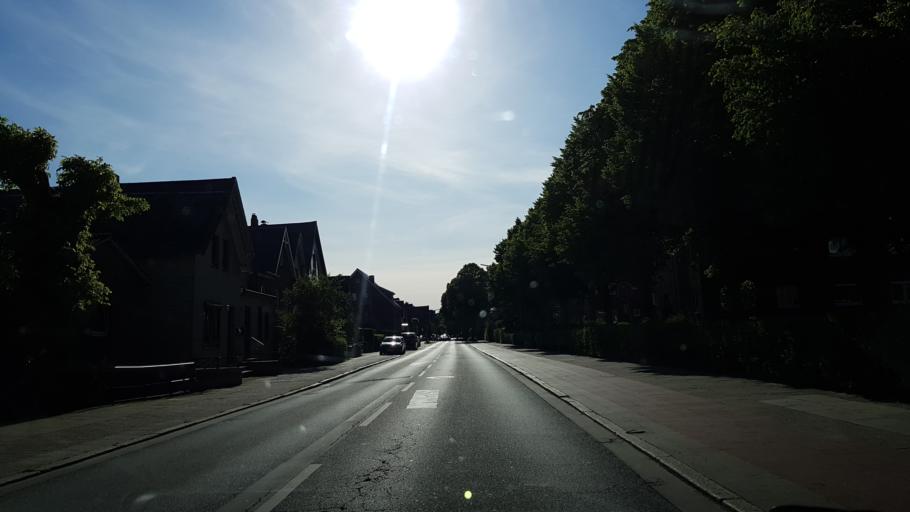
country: DE
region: Hamburg
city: Altona
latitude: 53.5336
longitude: 9.8752
